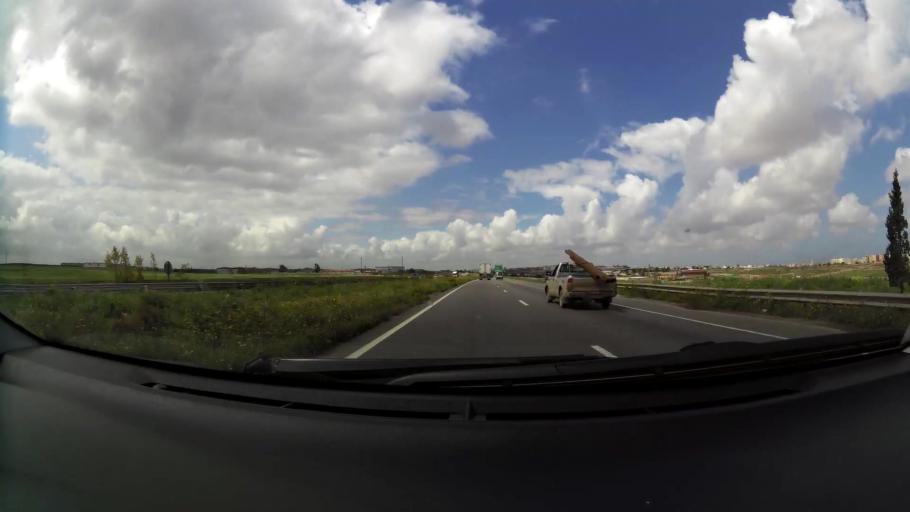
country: MA
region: Grand Casablanca
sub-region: Casablanca
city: Casablanca
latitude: 33.5317
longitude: -7.5592
